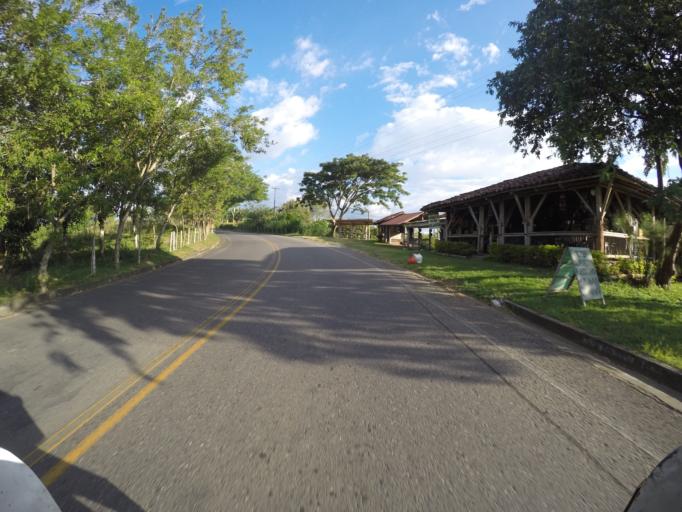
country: CO
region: Valle del Cauca
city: Alcala
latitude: 4.6816
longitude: -75.7984
